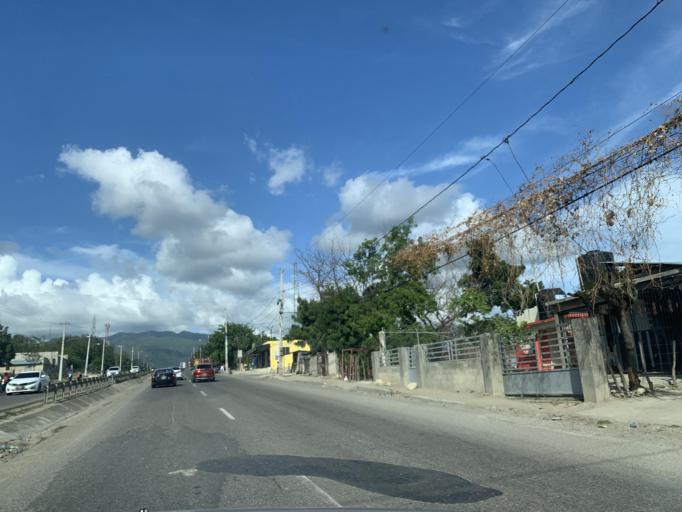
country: DO
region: Santiago
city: Villa Gonzalez
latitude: 19.5497
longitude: -70.8325
